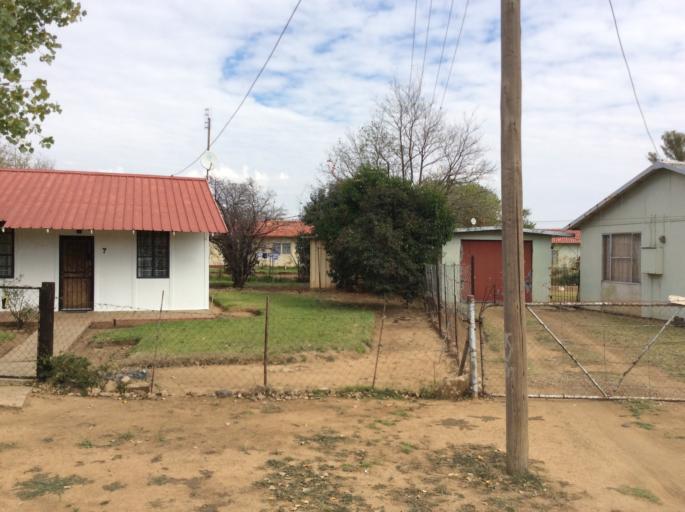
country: LS
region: Mafeteng
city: Mafeteng
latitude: -29.7290
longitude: 27.0259
